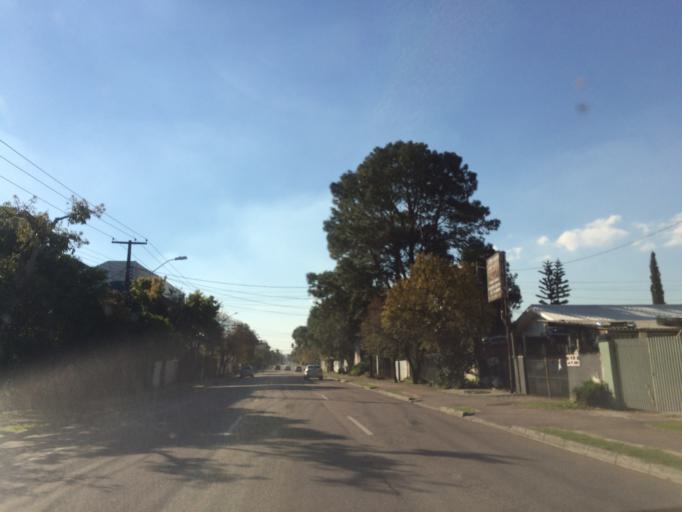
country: BR
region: Parana
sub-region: Sao Jose Dos Pinhais
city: Sao Jose dos Pinhais
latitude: -25.4910
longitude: -49.2414
